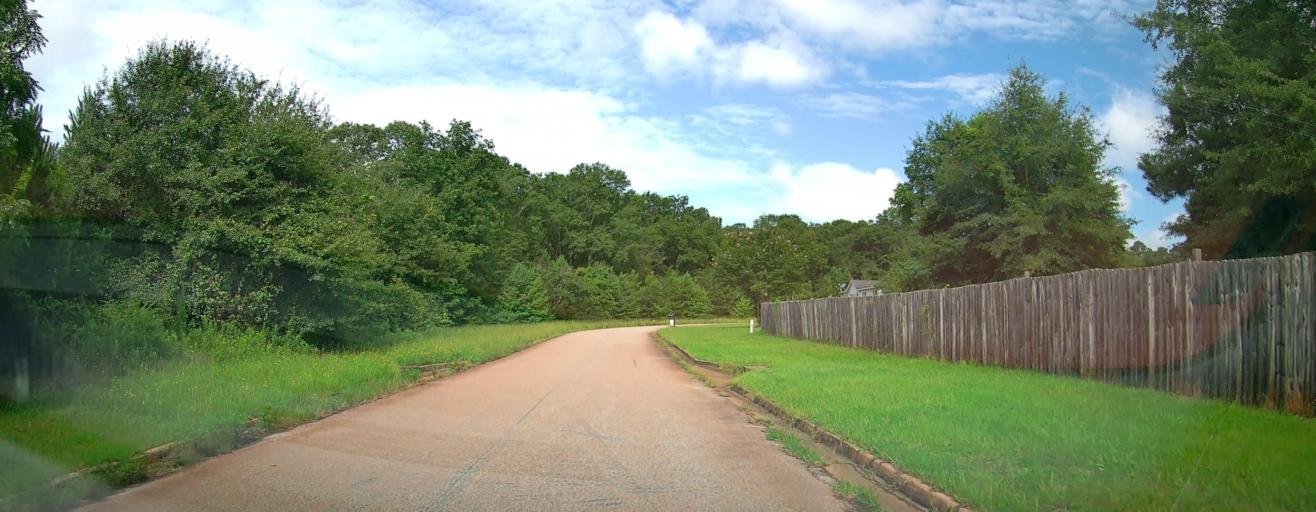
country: US
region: Georgia
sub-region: Houston County
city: Centerville
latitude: 32.6448
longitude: -83.7207
